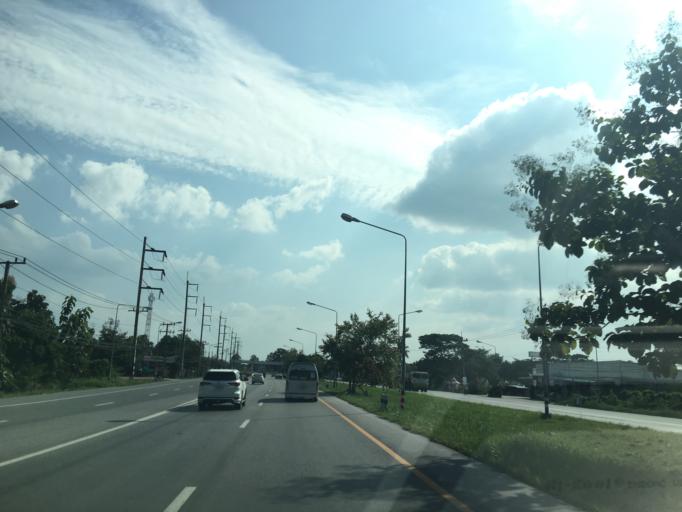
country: TH
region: Chiang Rai
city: Mae Lao
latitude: 19.7230
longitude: 99.7161
